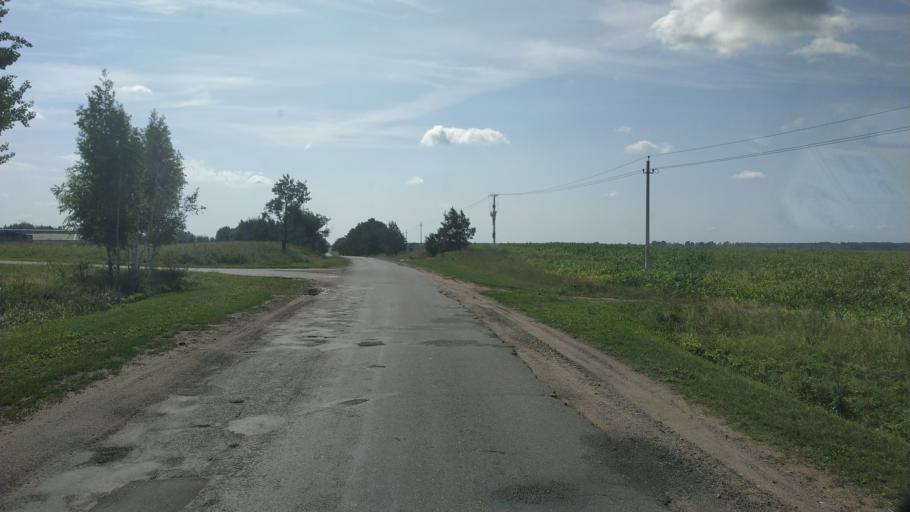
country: BY
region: Mogilev
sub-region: Mahilyowski Rayon
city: Veyno
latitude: 53.7846
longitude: 30.4355
